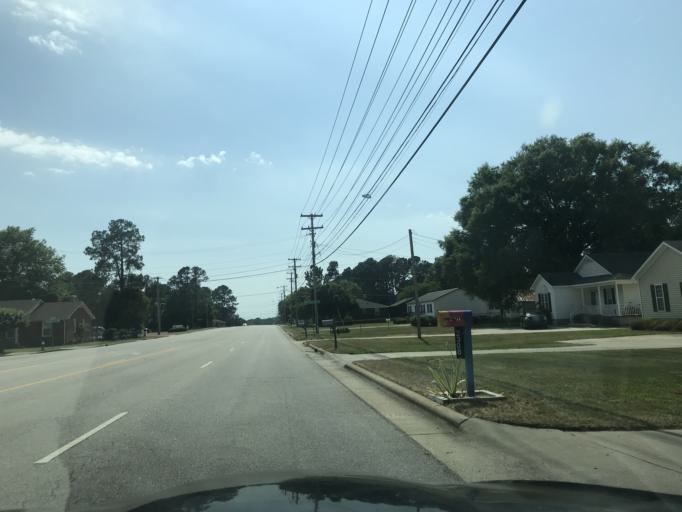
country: US
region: North Carolina
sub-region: Wilson County
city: Wilson
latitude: 35.7113
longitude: -77.9393
